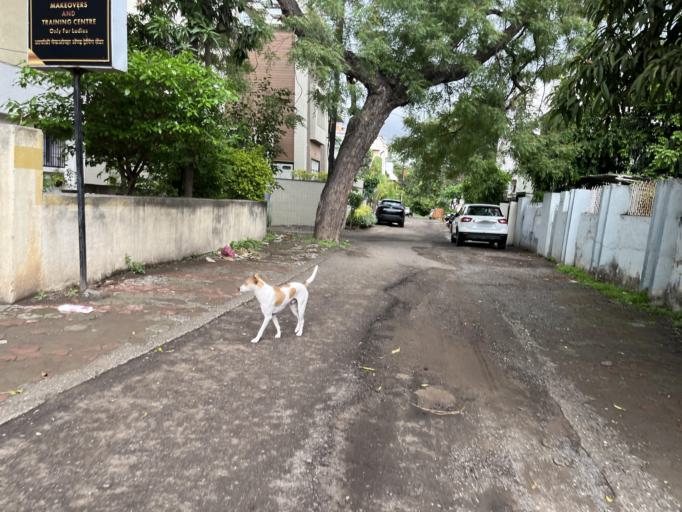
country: IN
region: Maharashtra
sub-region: Aurangabad Division
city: Aurangabad
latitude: 19.8808
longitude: 75.3711
